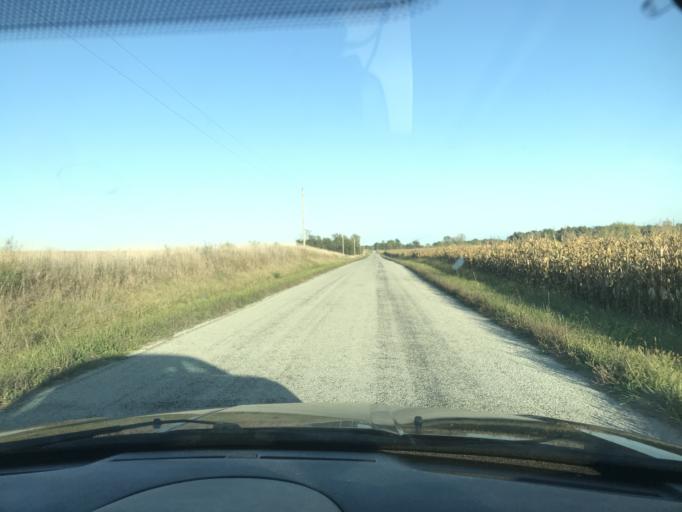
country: US
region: Ohio
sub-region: Logan County
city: West Liberty
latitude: 40.2338
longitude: -83.8394
